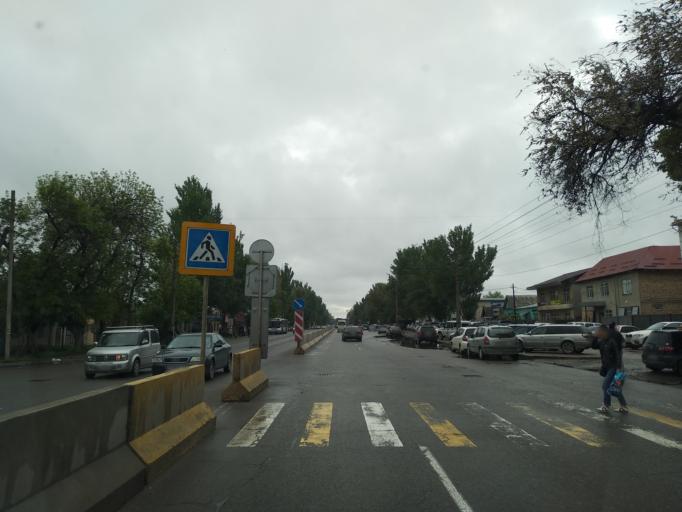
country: KG
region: Chuy
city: Lebedinovka
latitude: 42.8887
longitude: 74.6476
